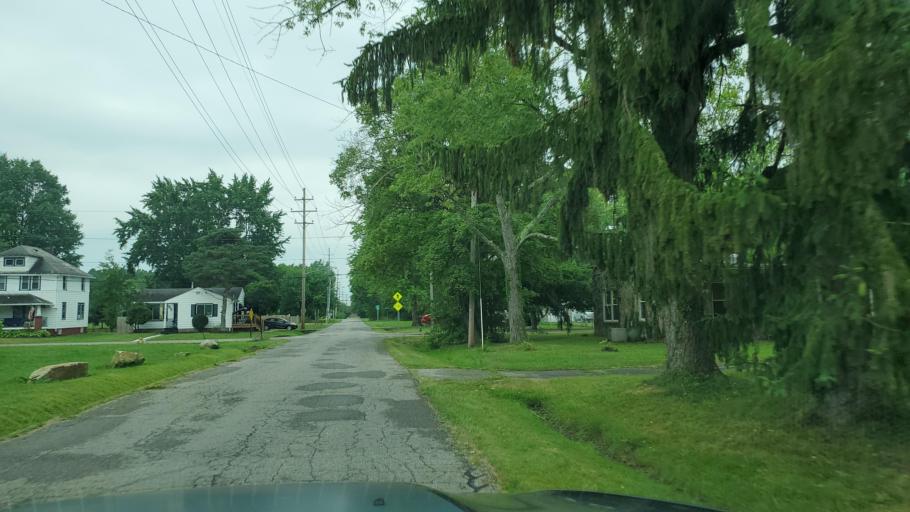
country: US
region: Ohio
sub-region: Trumbull County
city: Warren
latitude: 41.2564
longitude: -80.8135
